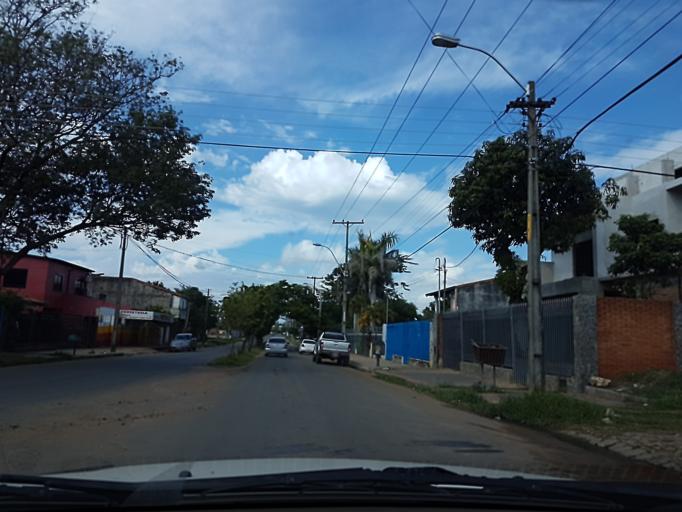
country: PY
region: Central
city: Colonia Mariano Roque Alonso
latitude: -25.2236
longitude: -57.5400
